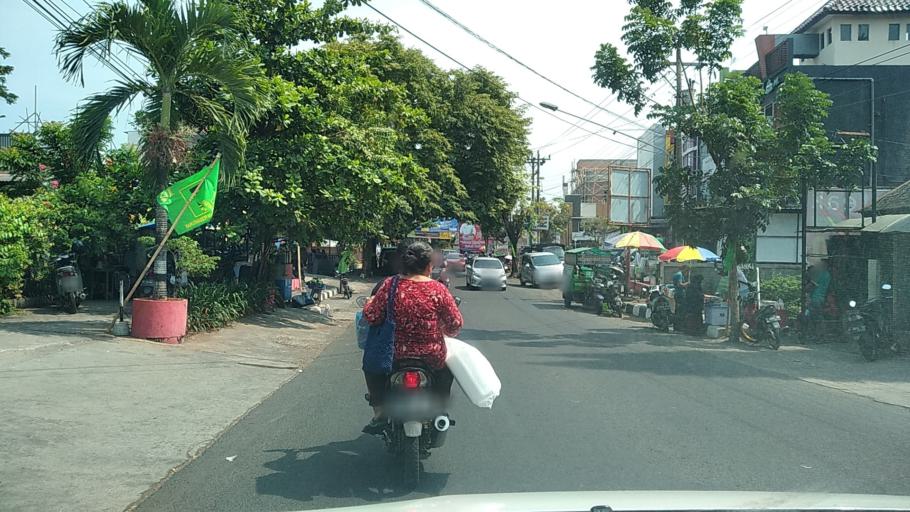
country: ID
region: Central Java
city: Ungaran
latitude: -7.0671
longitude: 110.4183
